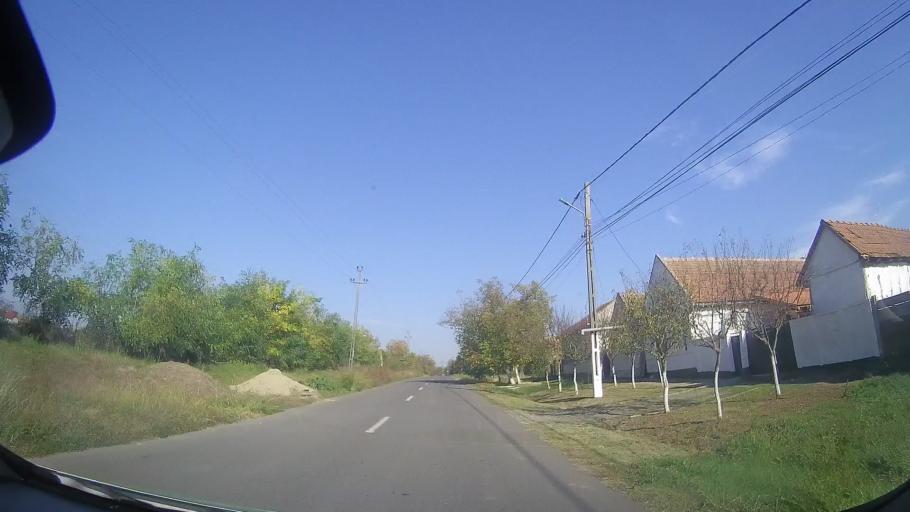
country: RO
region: Timis
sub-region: Comuna Topolovatu Mare
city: Topolovatu Mare
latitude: 45.8159
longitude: 21.5806
